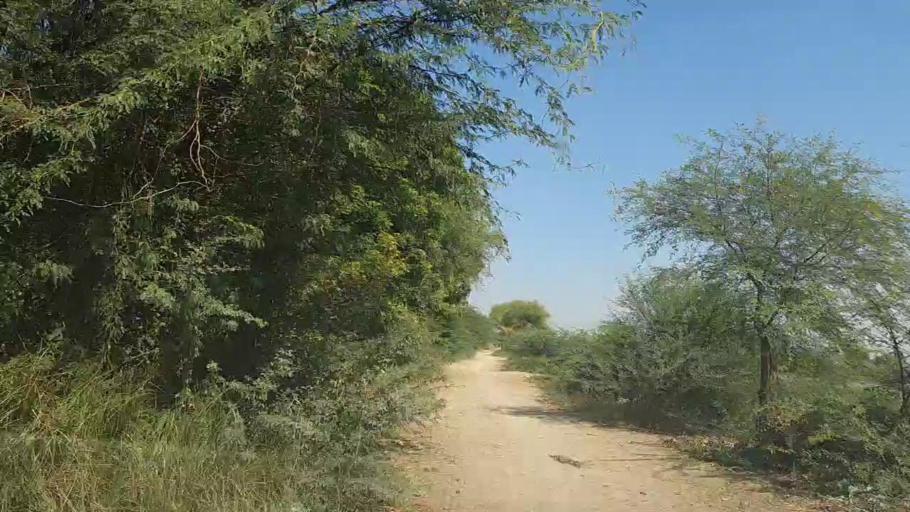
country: PK
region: Sindh
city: Thatta
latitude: 24.7836
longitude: 67.9728
